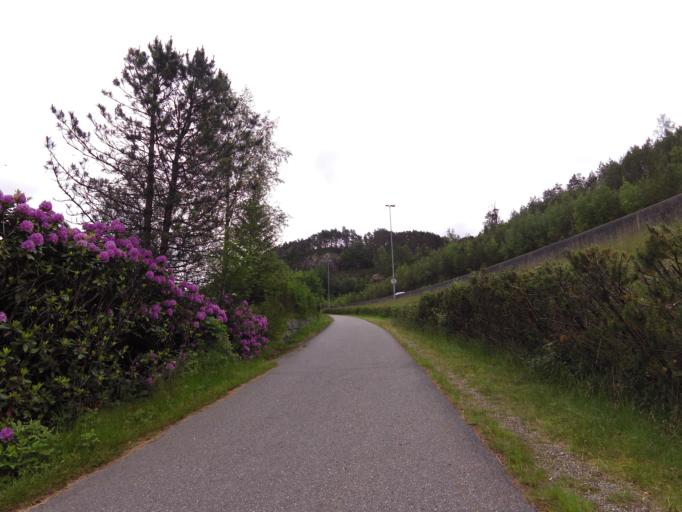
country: NO
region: Vest-Agder
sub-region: Flekkefjord
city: Flekkefjord
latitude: 58.2966
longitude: 6.6808
